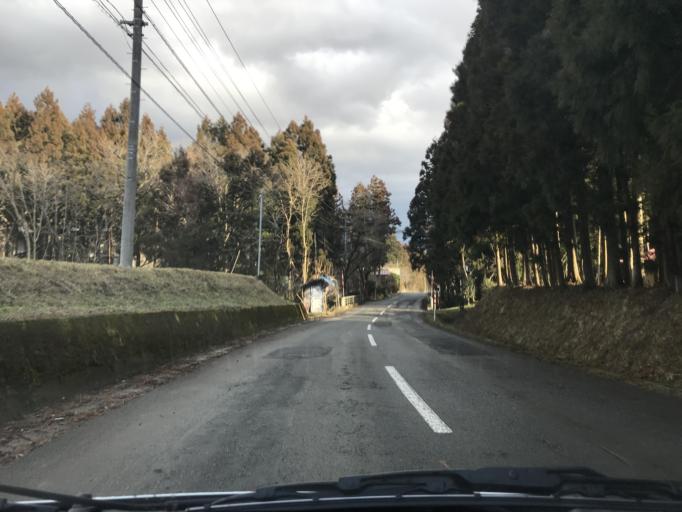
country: JP
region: Iwate
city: Mizusawa
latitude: 39.0616
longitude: 141.0342
